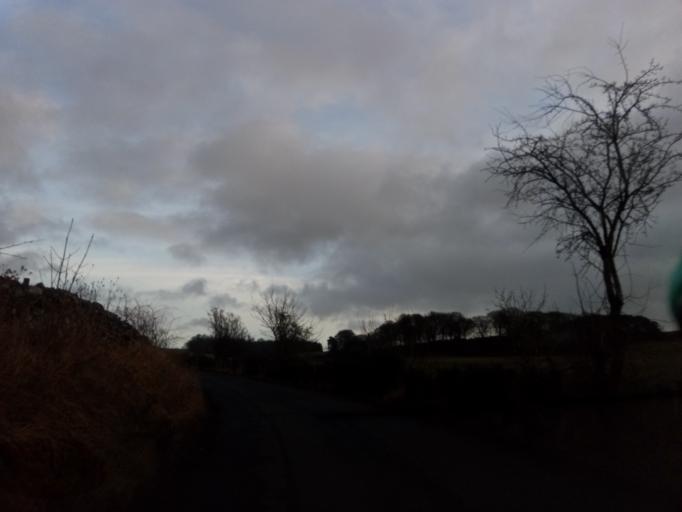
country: GB
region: Scotland
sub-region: The Scottish Borders
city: Selkirk
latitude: 55.5620
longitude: -2.7974
